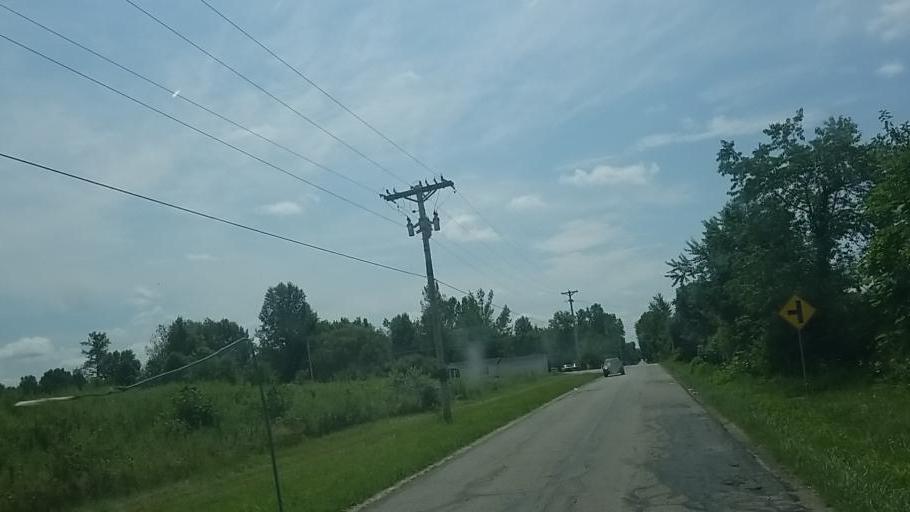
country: US
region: Ohio
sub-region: Franklin County
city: New Albany
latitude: 40.0445
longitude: -82.7680
